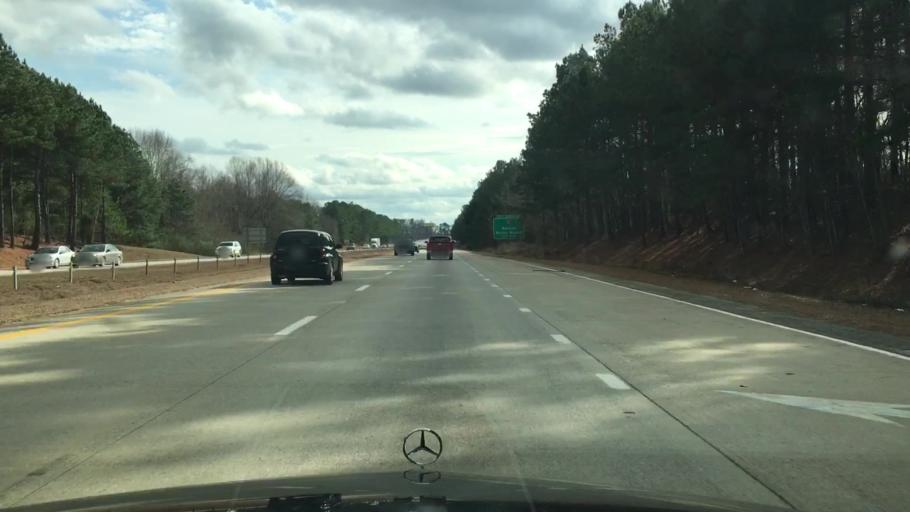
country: US
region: North Carolina
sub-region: Johnston County
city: Benson
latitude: 35.4186
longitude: -78.5282
